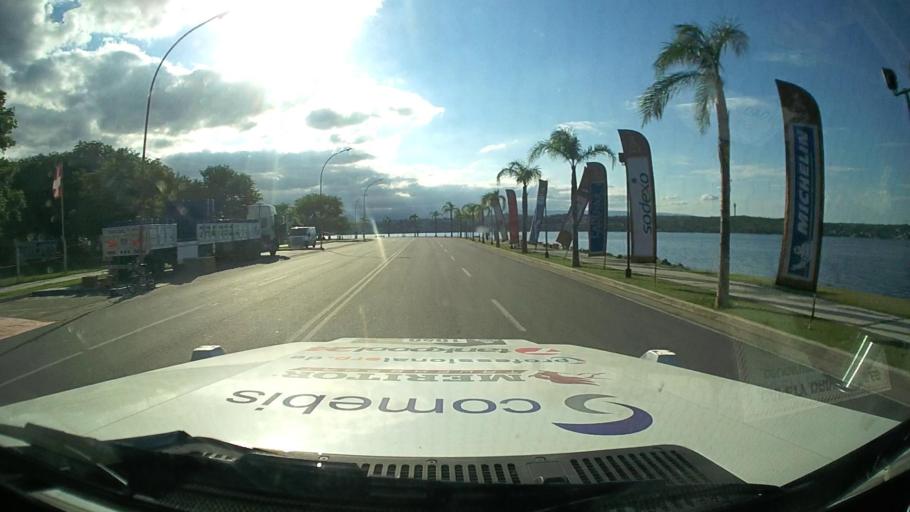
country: AR
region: Cordoba
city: Villa Carlos Paz
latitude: -31.3957
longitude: -64.4745
